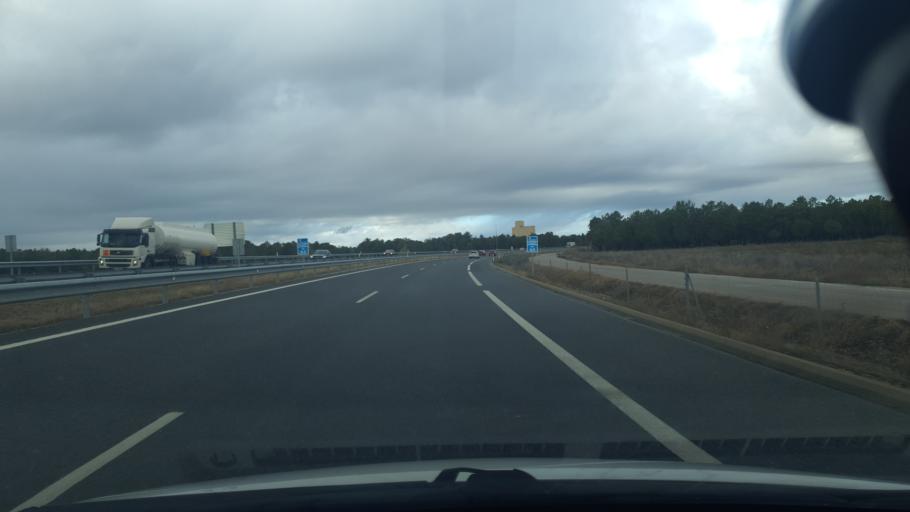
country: ES
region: Castille and Leon
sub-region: Provincia de Segovia
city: Sanchonuno
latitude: 41.3255
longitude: -4.3136
